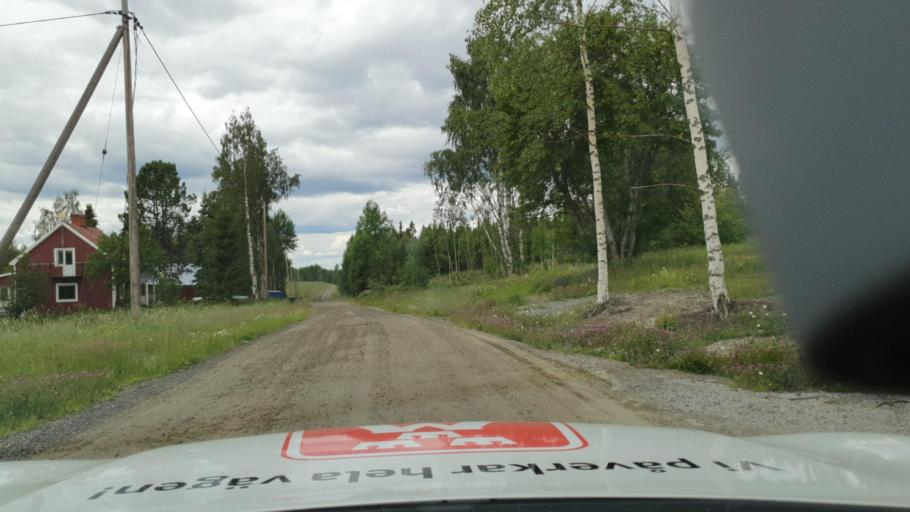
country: SE
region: Vaesterbotten
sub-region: Bjurholms Kommun
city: Bjurholm
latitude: 63.7915
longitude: 19.1026
